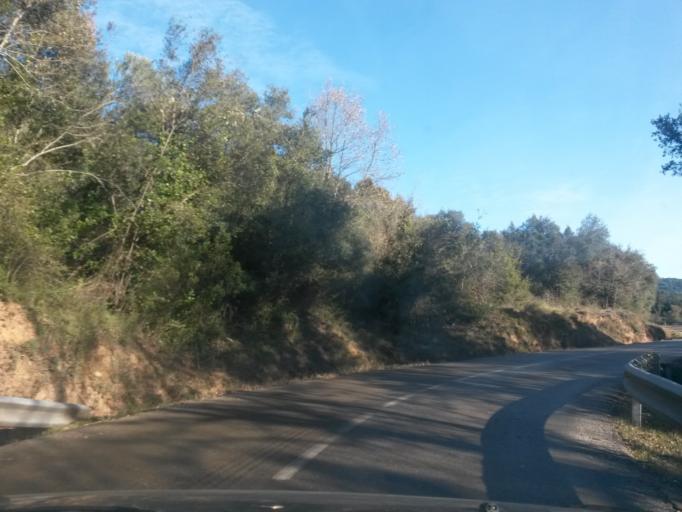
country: ES
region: Catalonia
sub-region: Provincia de Girona
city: la Cellera de Ter
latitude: 42.0166
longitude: 2.6691
